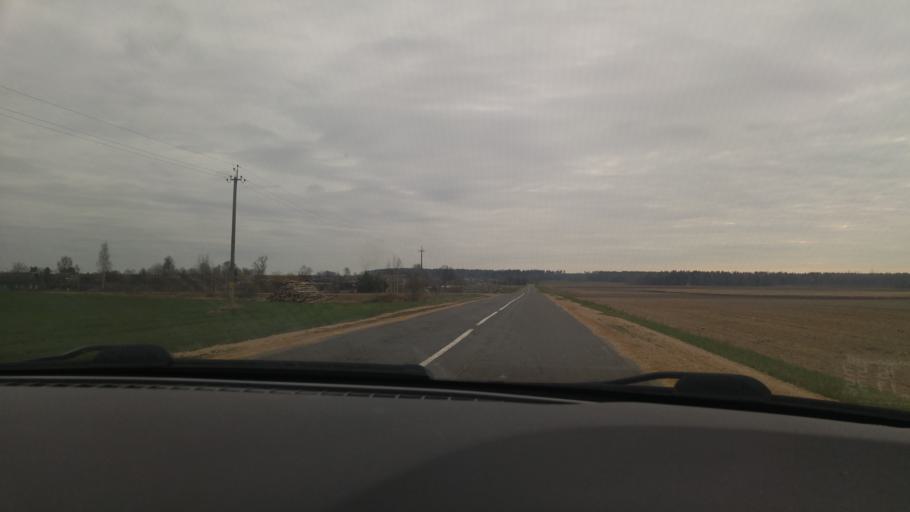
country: BY
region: Minsk
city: Chervyen'
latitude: 53.7242
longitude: 28.2654
